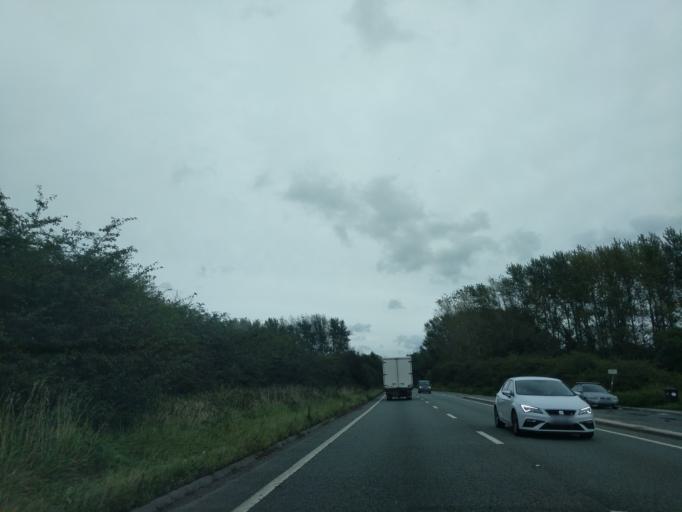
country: GB
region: England
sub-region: Cheshire East
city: Weston
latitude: 53.0701
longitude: -2.3714
